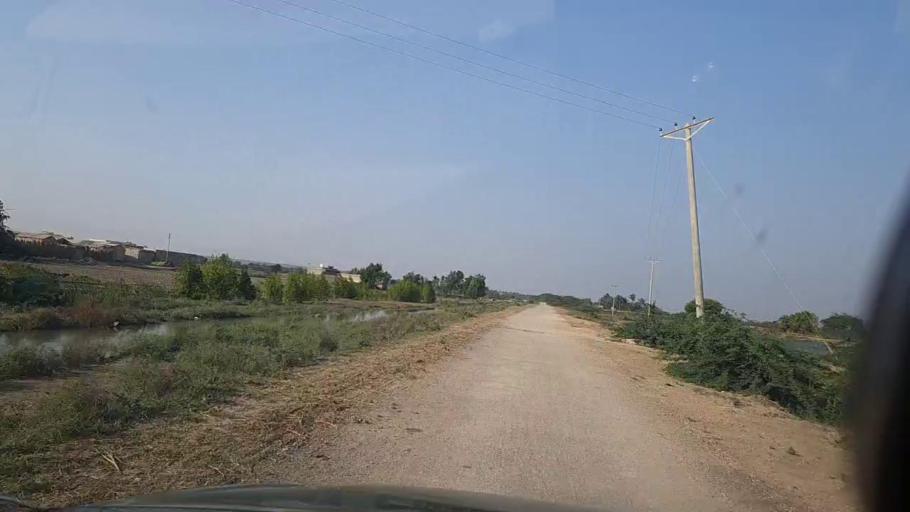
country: PK
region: Sindh
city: Thatta
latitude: 24.6130
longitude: 67.8763
